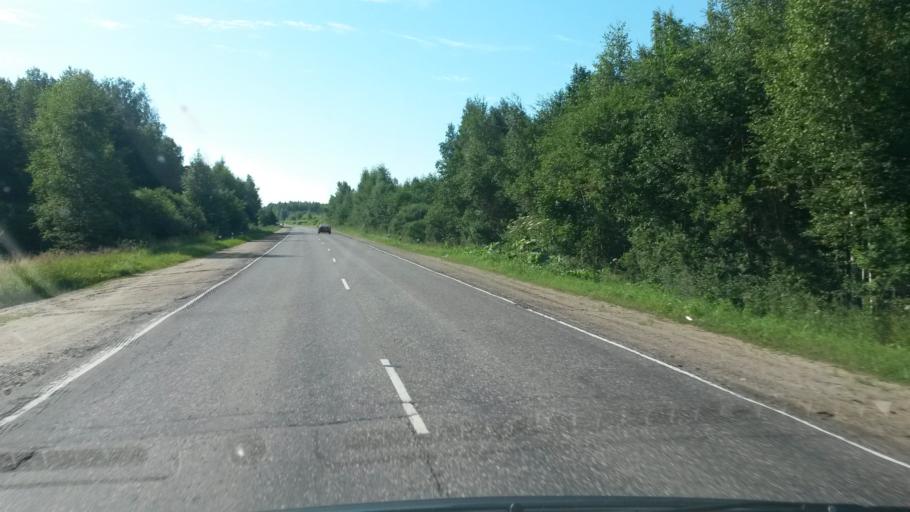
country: RU
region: Ivanovo
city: Novo-Talitsy
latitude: 57.0375
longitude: 40.7453
